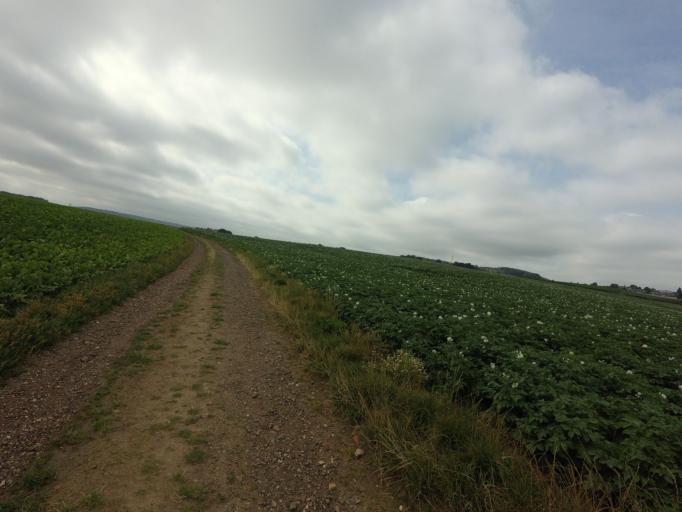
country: NL
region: Limburg
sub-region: Gemeente Simpelveld
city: Simpelveld
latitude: 50.7897
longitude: 5.9750
